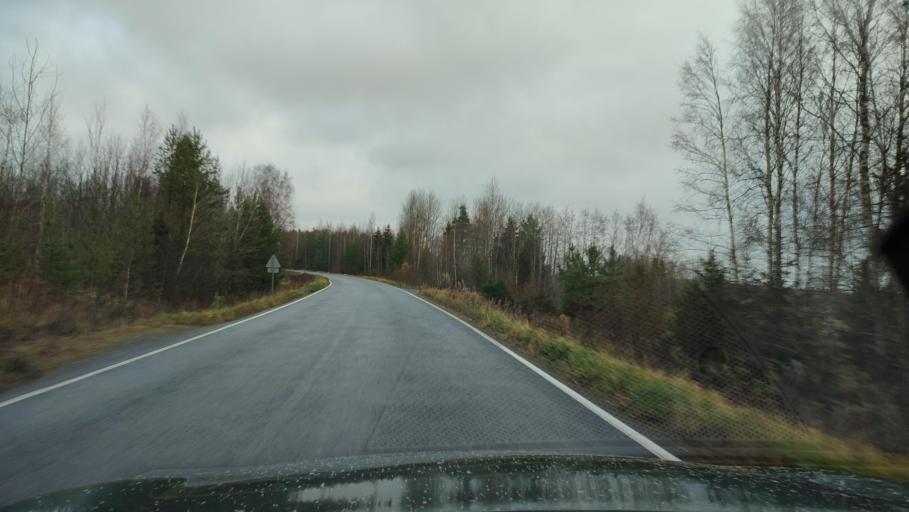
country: FI
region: Southern Ostrobothnia
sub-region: Suupohja
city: Karijoki
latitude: 62.3500
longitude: 21.5440
